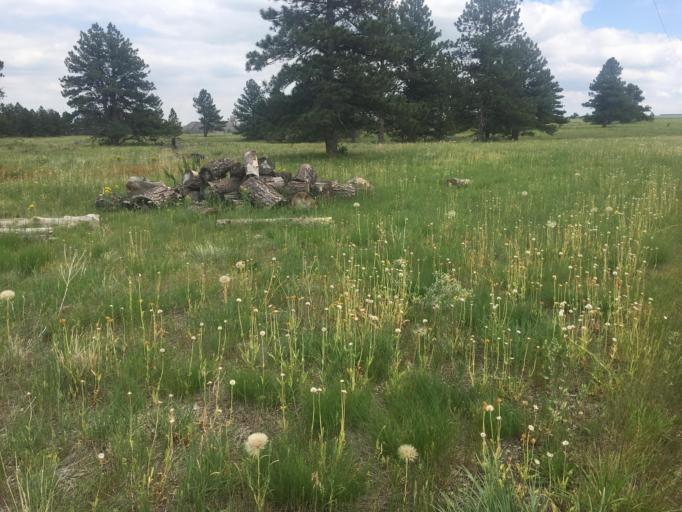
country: US
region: Colorado
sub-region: Boulder County
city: Superior
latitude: 39.9159
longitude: -105.2518
